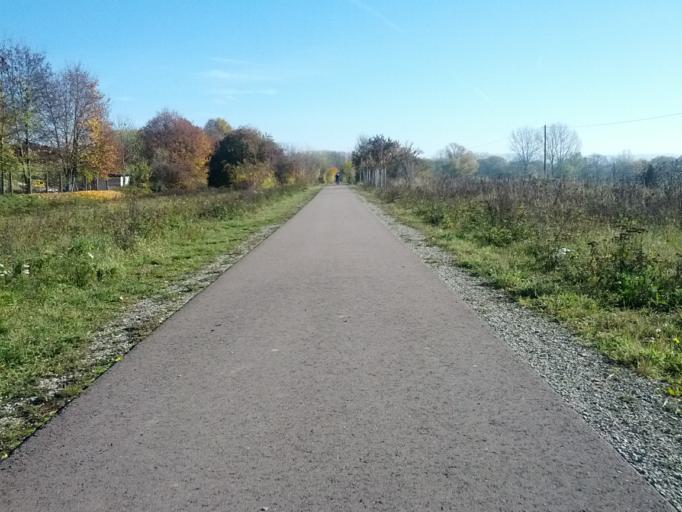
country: DE
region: Thuringia
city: Friedrichswerth
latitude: 50.9965
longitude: 10.5491
